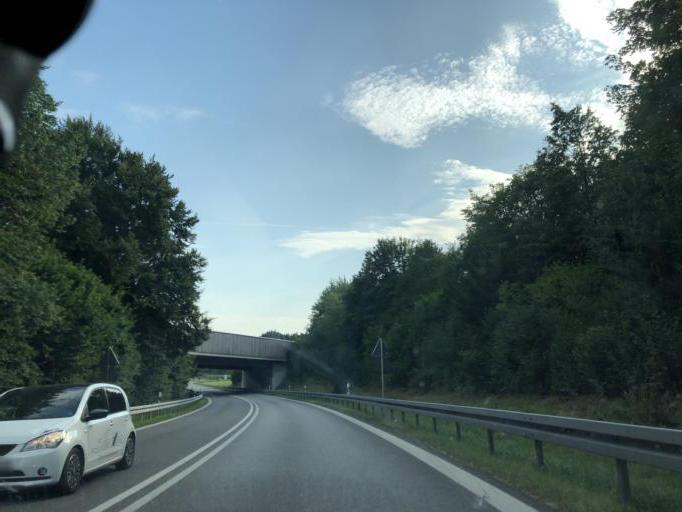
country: DE
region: Bavaria
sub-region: Swabia
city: Buchloe
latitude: 48.0275
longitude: 10.7282
